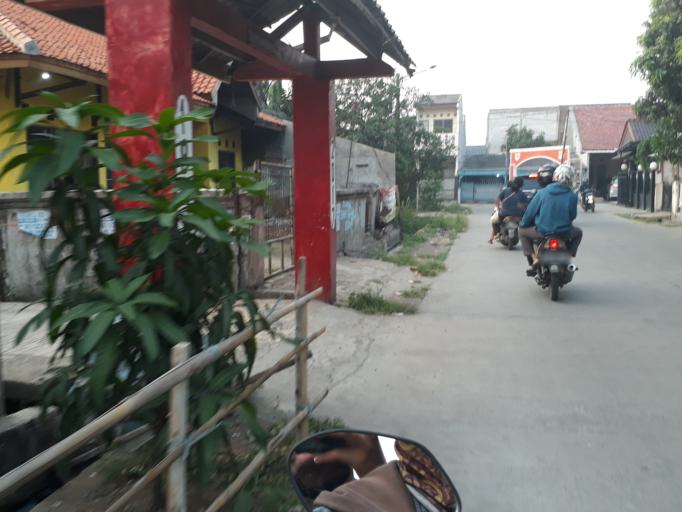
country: ID
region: West Java
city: Bekasi
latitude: -6.2414
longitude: 107.0390
